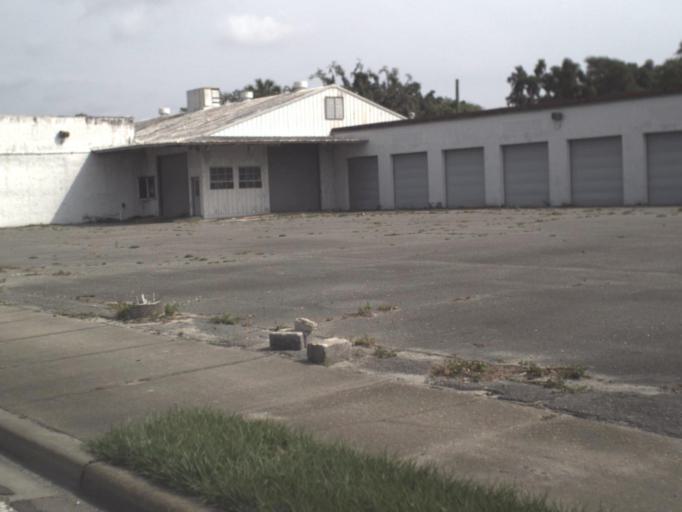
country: US
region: Florida
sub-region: Clay County
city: Green Cove Springs
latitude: 29.9970
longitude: -81.6806
